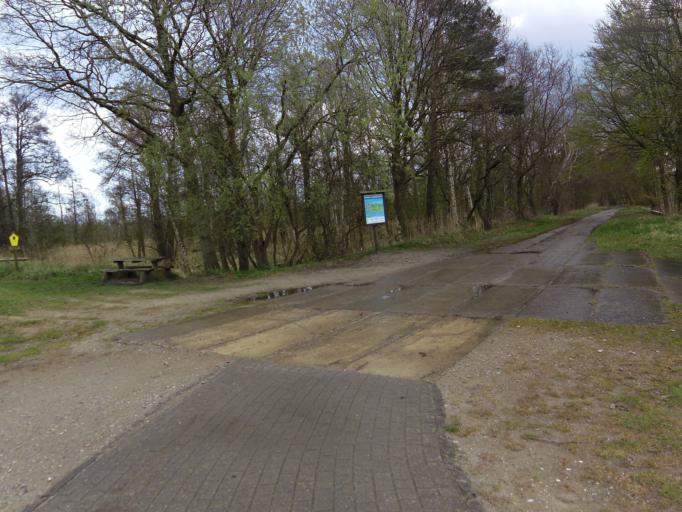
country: DE
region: Mecklenburg-Vorpommern
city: Zingst
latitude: 54.4398
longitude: 12.7797
